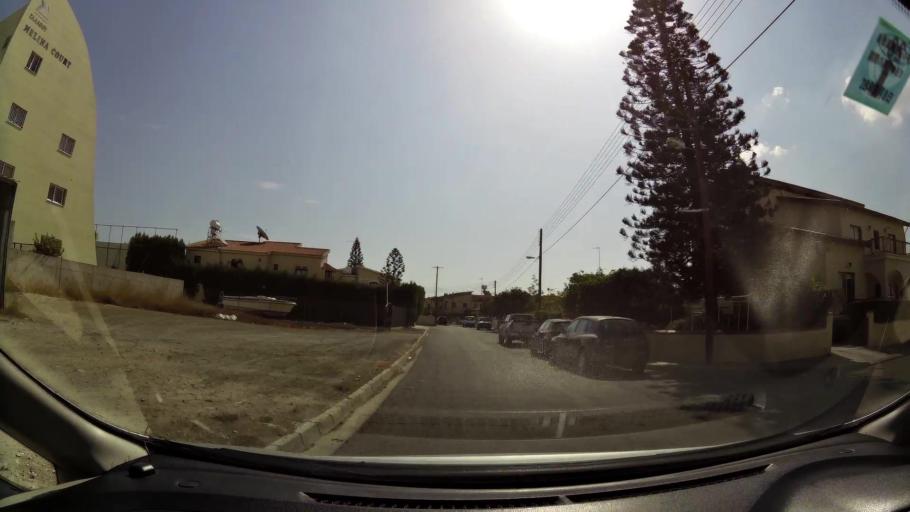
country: CY
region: Larnaka
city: Aradippou
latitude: 34.9413
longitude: 33.5882
